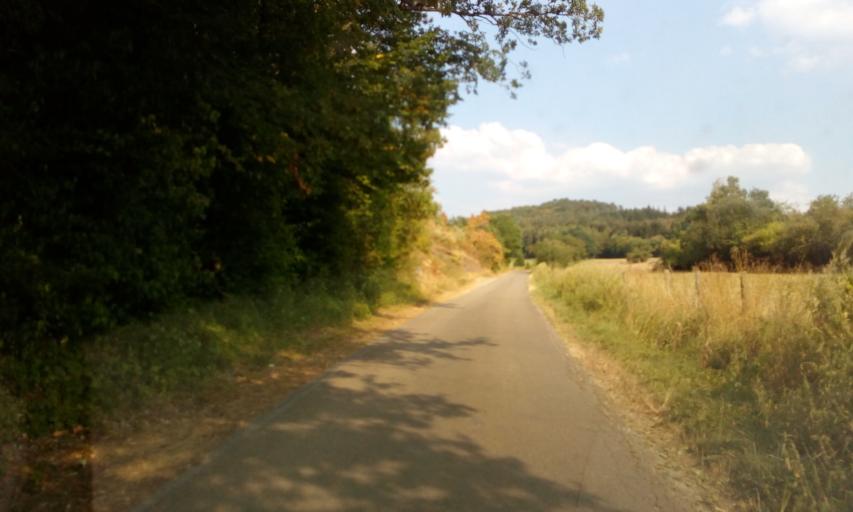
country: BE
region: Wallonia
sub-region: Province du Luxembourg
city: Tellin
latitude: 50.1093
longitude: 5.2137
